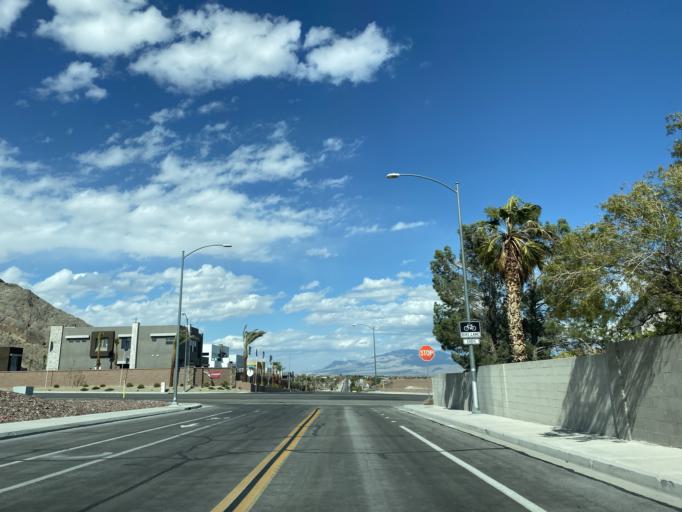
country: US
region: Nevada
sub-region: Clark County
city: Summerlin South
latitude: 36.2327
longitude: -115.3086
